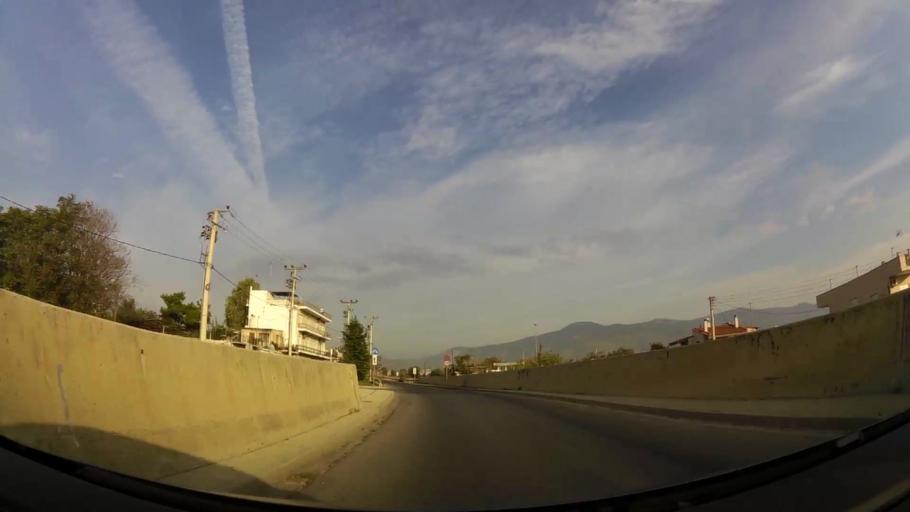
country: GR
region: Attica
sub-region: Nomarchia Dytikis Attikis
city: Zefyri
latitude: 38.0683
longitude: 23.7119
